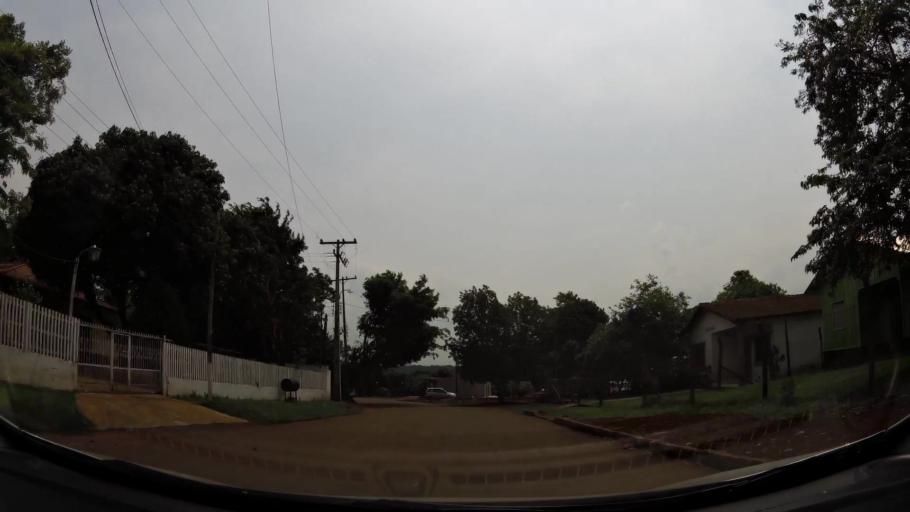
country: BR
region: Parana
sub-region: Foz Do Iguacu
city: Foz do Iguacu
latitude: -25.5709
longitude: -54.6150
